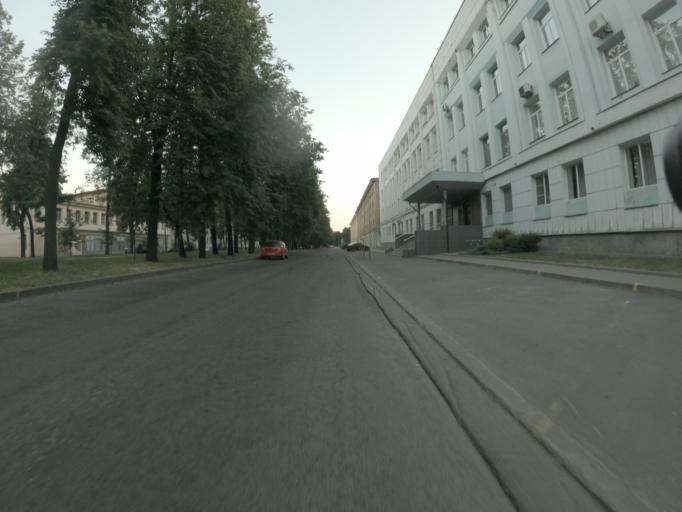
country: RU
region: St.-Petersburg
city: Centralniy
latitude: 59.9219
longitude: 30.4167
